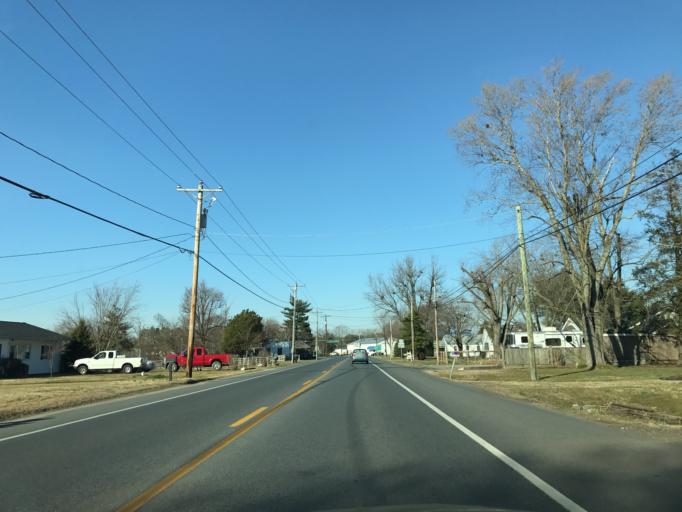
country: US
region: Maryland
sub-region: Caroline County
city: Denton
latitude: 38.9034
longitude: -75.8149
